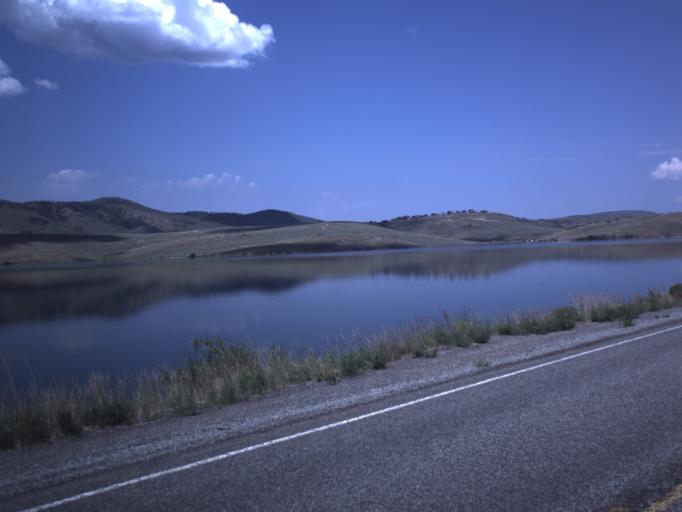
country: US
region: Utah
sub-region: Carbon County
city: Helper
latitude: 39.7709
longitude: -111.1398
